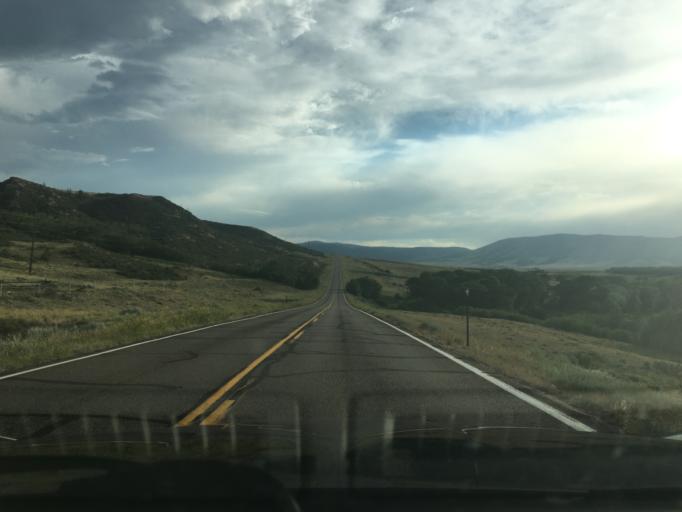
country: US
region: Wyoming
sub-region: Albany County
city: Laramie
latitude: 41.2834
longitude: -106.0568
